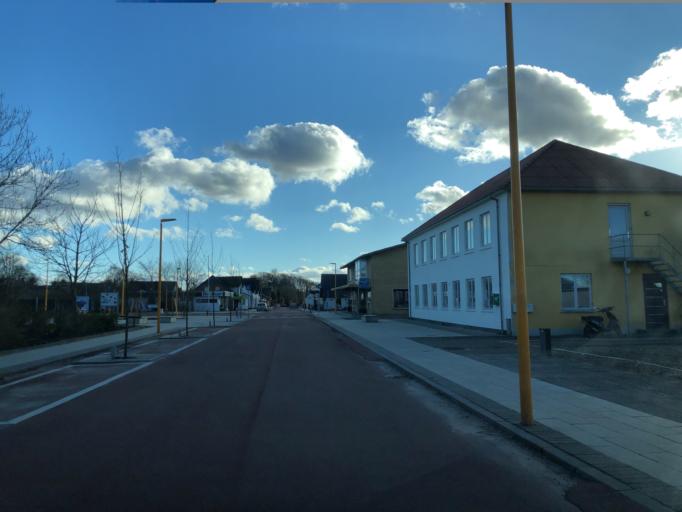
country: DK
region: Central Jutland
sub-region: Viborg Kommune
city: Karup
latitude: 56.3079
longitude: 9.1656
